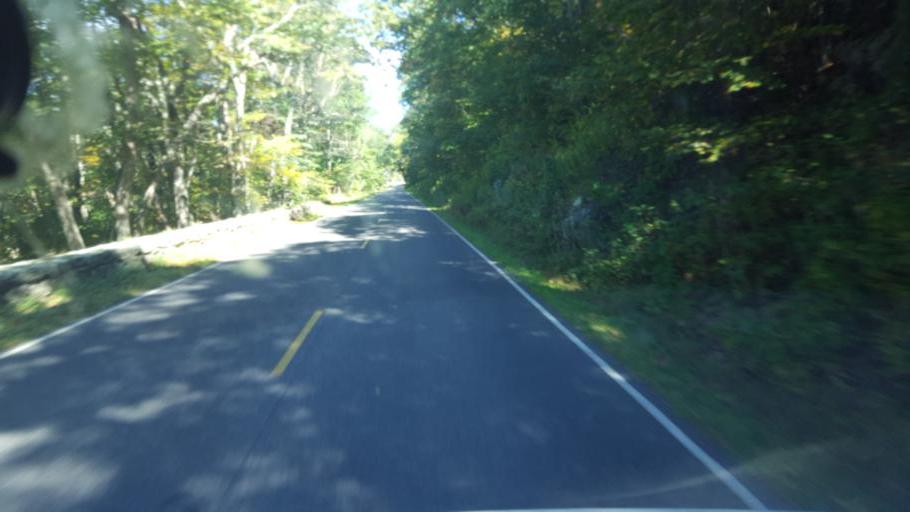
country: US
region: Virginia
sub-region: Page County
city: Stanley
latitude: 38.4732
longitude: -78.4572
